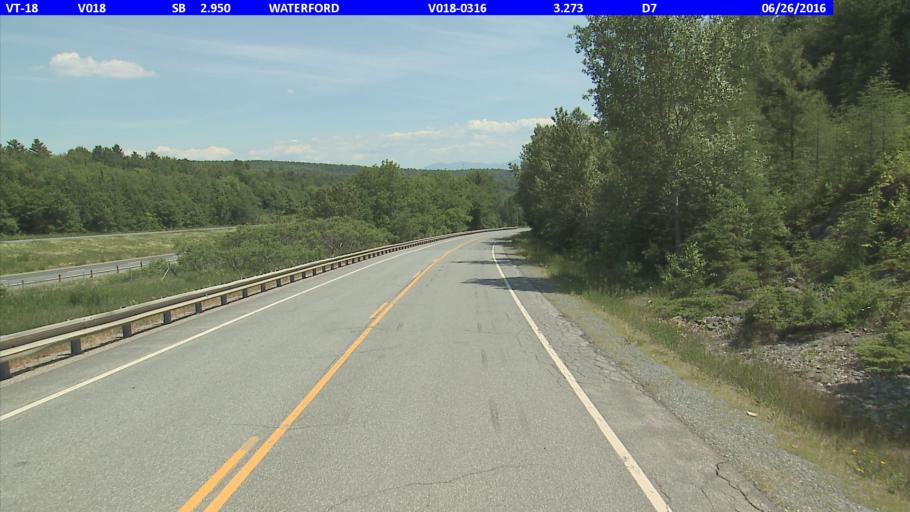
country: US
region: Vermont
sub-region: Caledonia County
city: Saint Johnsbury
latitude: 44.3772
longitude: -71.9152
